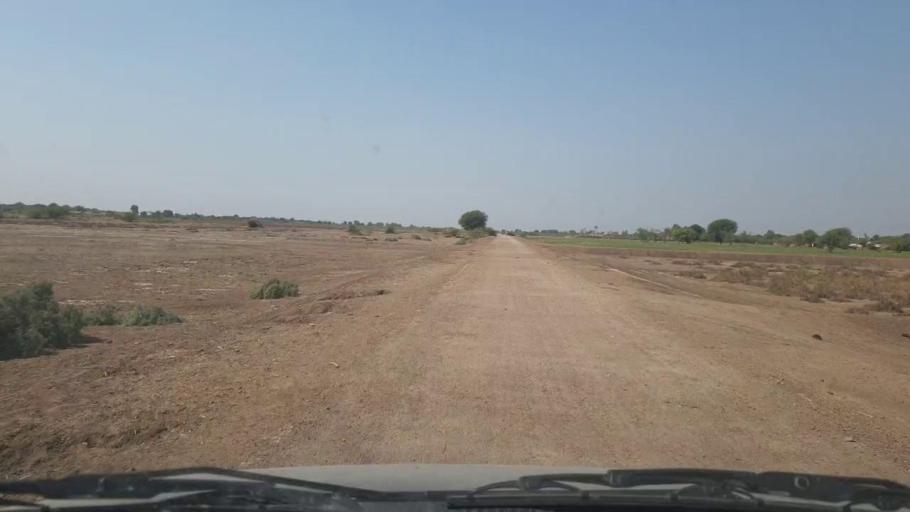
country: PK
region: Sindh
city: Samaro
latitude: 25.2402
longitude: 69.3331
